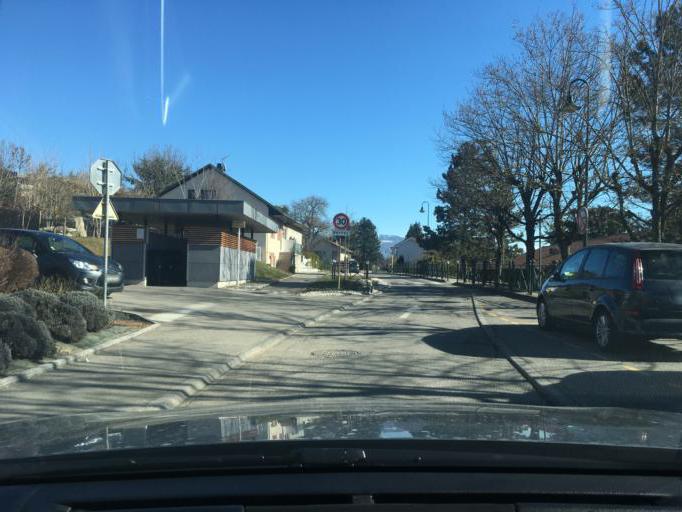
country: FR
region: Rhone-Alpes
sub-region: Departement de la Haute-Savoie
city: Vetraz-Monthoux
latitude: 46.1742
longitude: 6.2604
